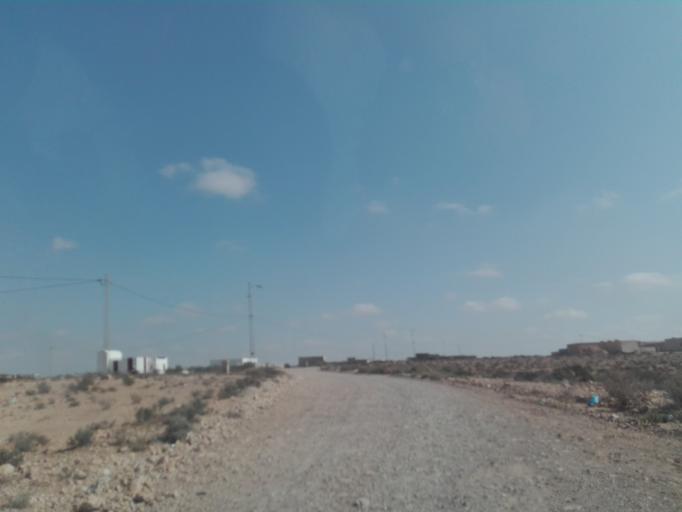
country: TN
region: Madanin
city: Medenine
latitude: 33.4287
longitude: 10.4060
